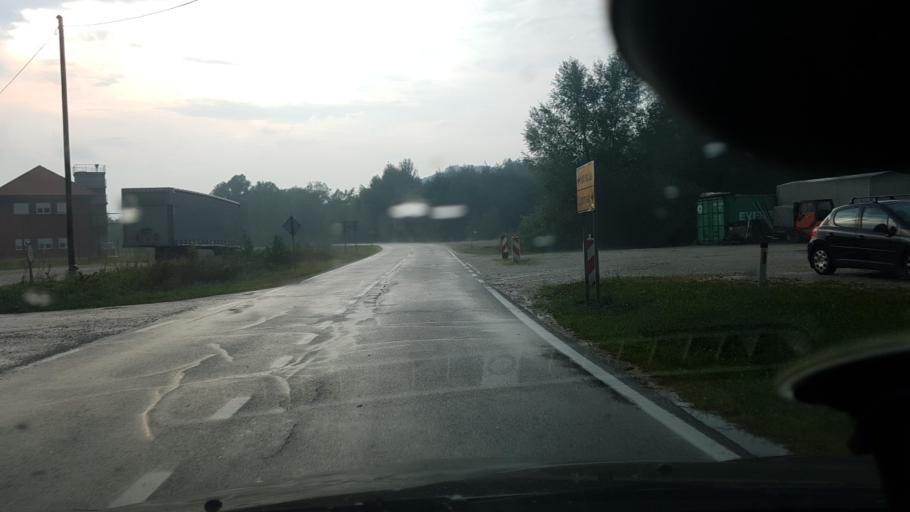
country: SI
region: Rogatec
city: Rogatec
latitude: 46.2217
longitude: 15.7219
